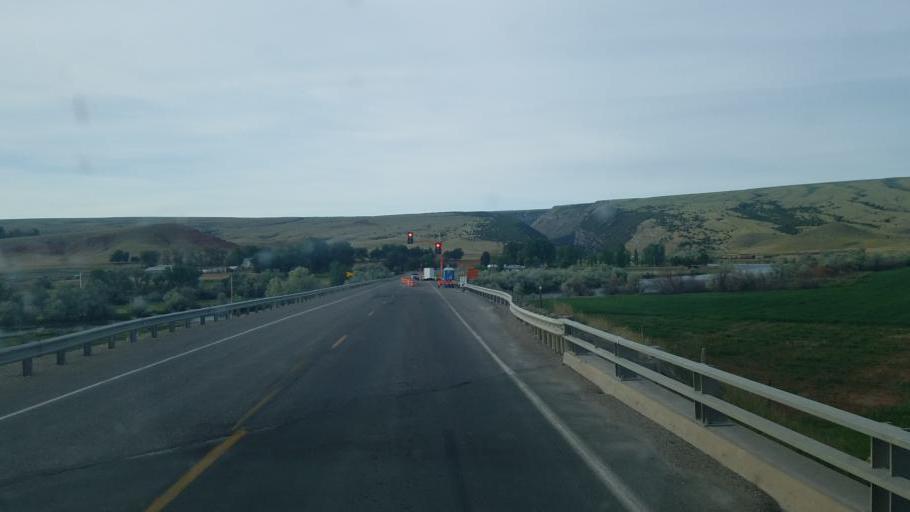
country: US
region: Wyoming
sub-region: Hot Springs County
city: Thermopolis
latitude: 43.5945
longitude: -108.2147
